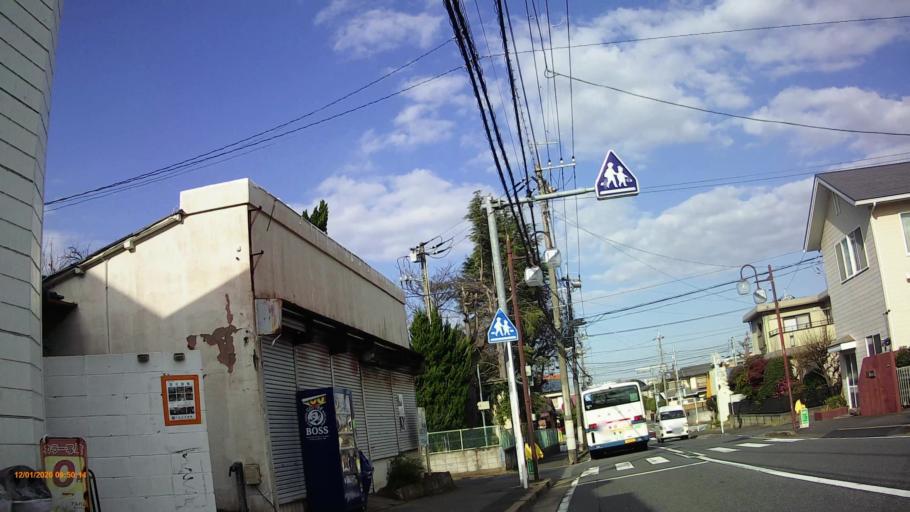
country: JP
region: Chiba
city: Yotsukaido
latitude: 35.6226
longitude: 140.1928
